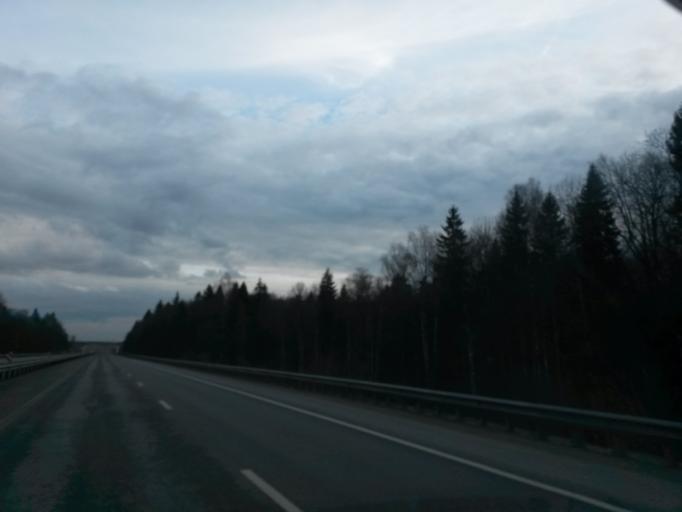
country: RU
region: Moskovskaya
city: Svatkovo
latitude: 56.3994
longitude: 38.3272
